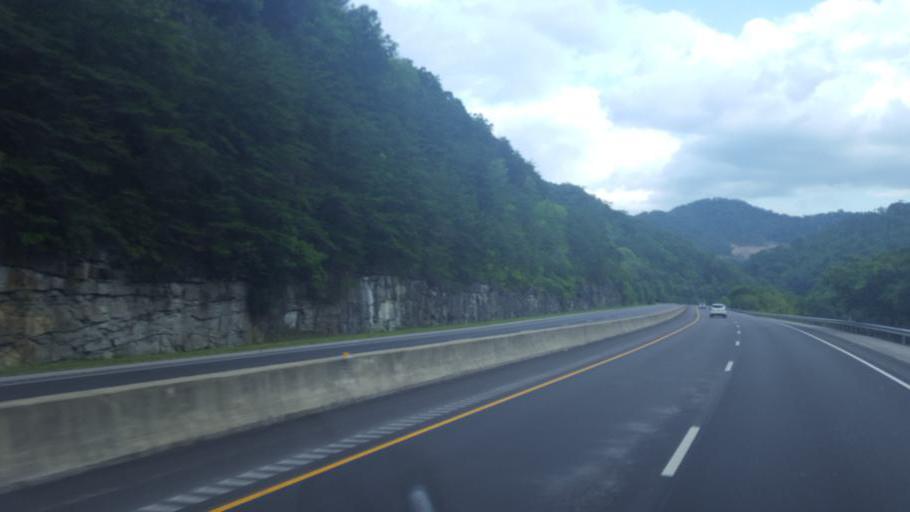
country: US
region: Kentucky
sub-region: Pike County
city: Pikeville
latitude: 37.3517
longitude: -82.5530
